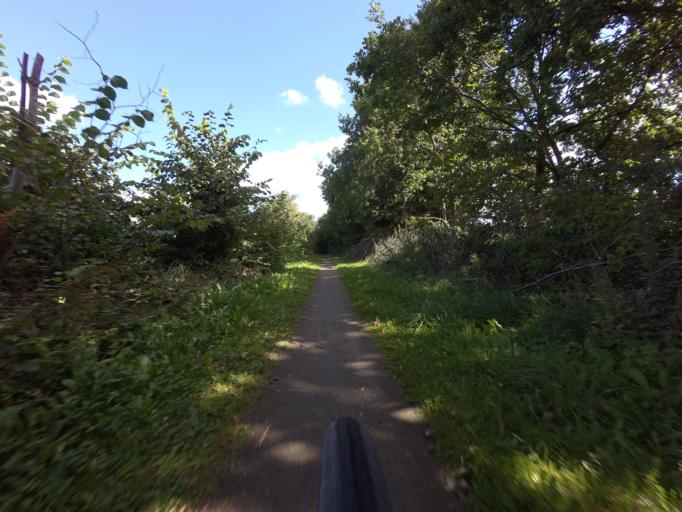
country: DK
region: South Denmark
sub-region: Vejle Kommune
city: Give
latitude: 55.9823
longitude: 9.2970
